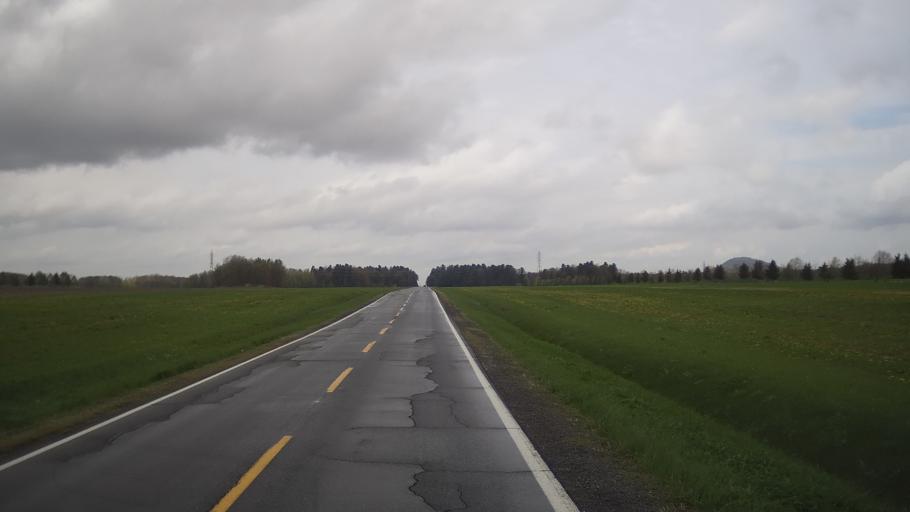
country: CA
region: Quebec
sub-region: Monteregie
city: Marieville
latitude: 45.3082
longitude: -73.1185
